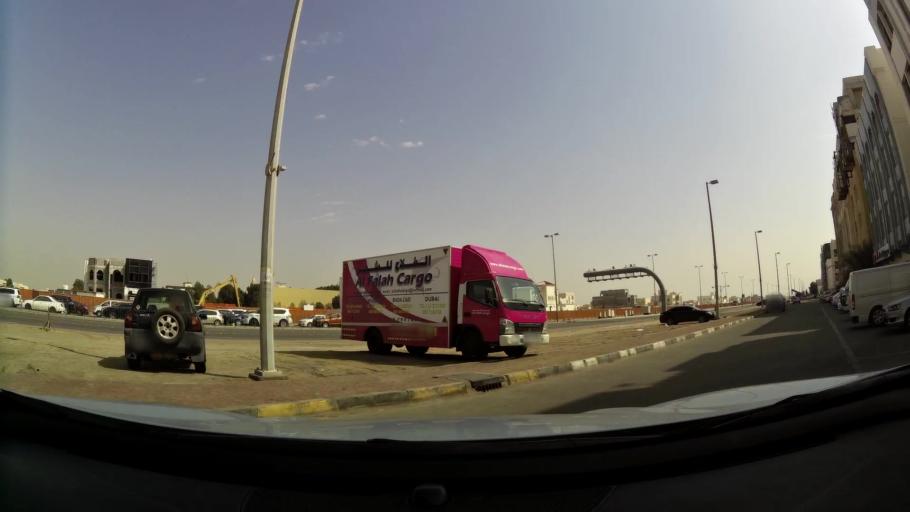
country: AE
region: Abu Dhabi
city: Abu Dhabi
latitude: 24.3376
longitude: 54.5383
